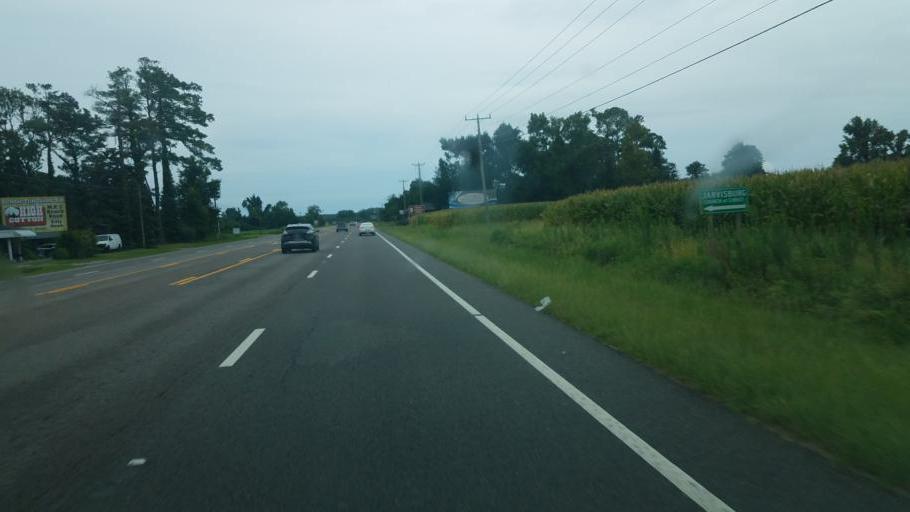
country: US
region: North Carolina
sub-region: Dare County
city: Southern Shores
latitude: 36.2015
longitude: -75.8652
